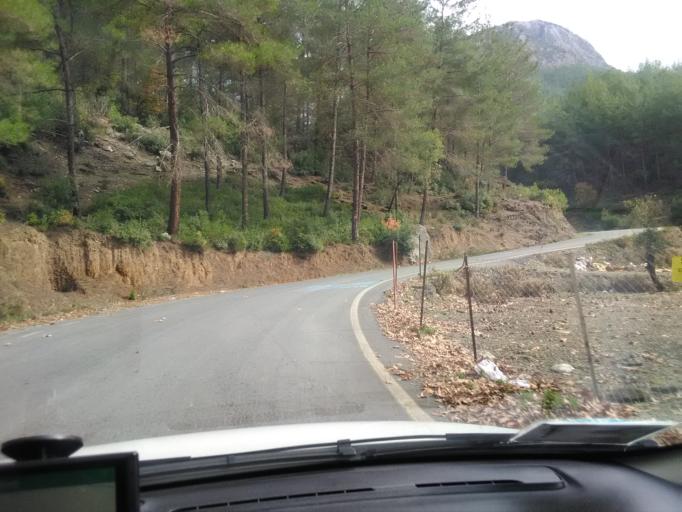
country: TR
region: Antalya
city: Gazipasa
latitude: 36.2456
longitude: 32.4126
